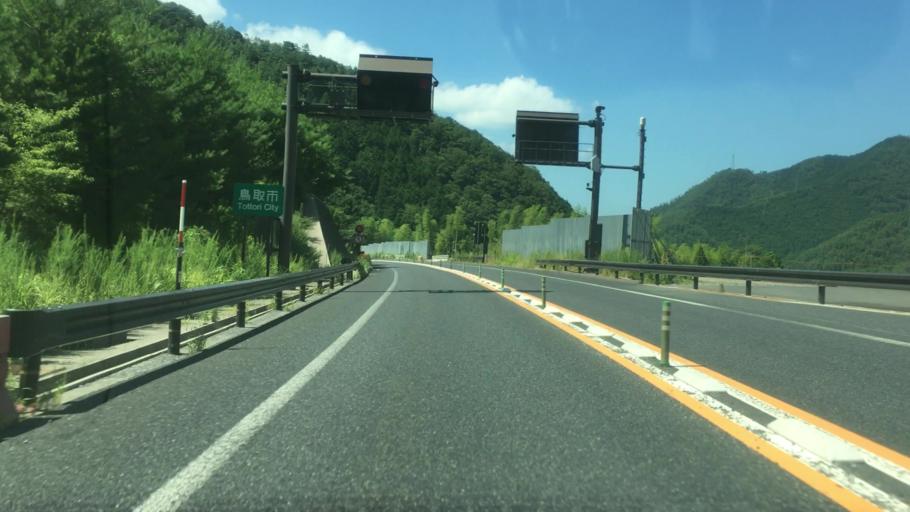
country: JP
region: Tottori
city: Tottori
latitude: 35.2991
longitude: 134.2026
